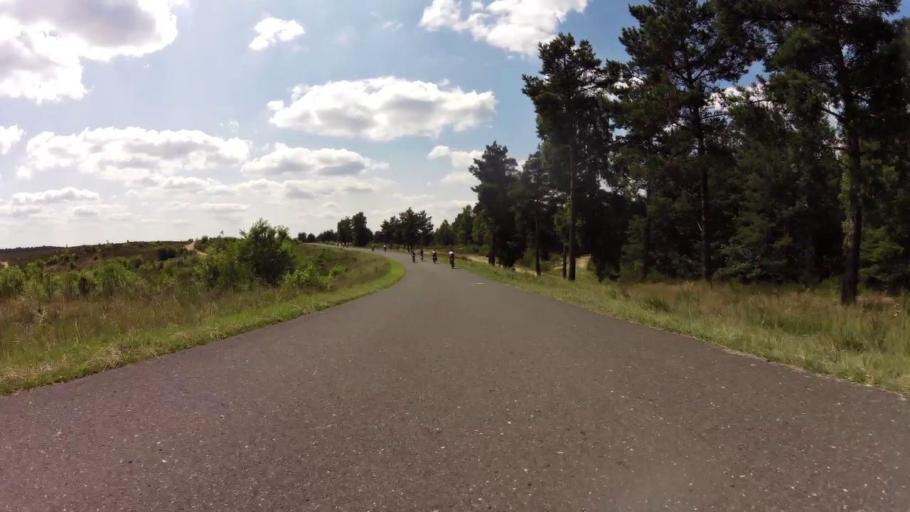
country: PL
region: West Pomeranian Voivodeship
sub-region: Powiat drawski
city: Drawsko Pomorskie
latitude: 53.4283
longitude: 15.7466
